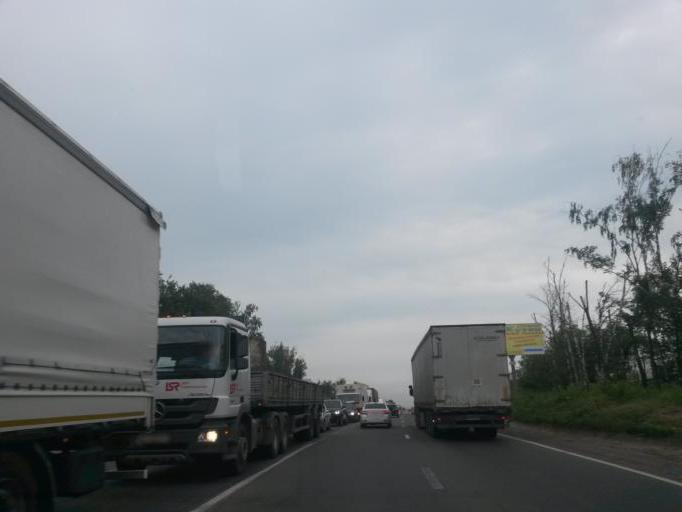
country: RU
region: Moskovskaya
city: Petrovskaya
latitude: 55.5561
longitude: 37.7751
